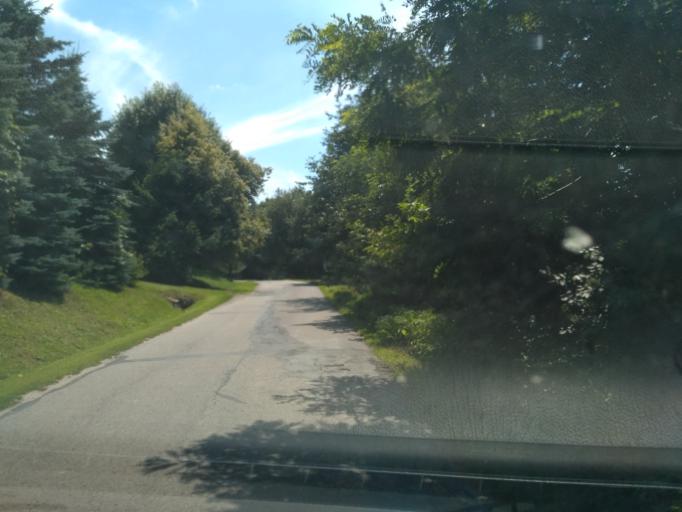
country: PL
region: Subcarpathian Voivodeship
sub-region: Powiat strzyzowski
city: Strzyzow
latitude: 49.8590
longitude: 21.7992
